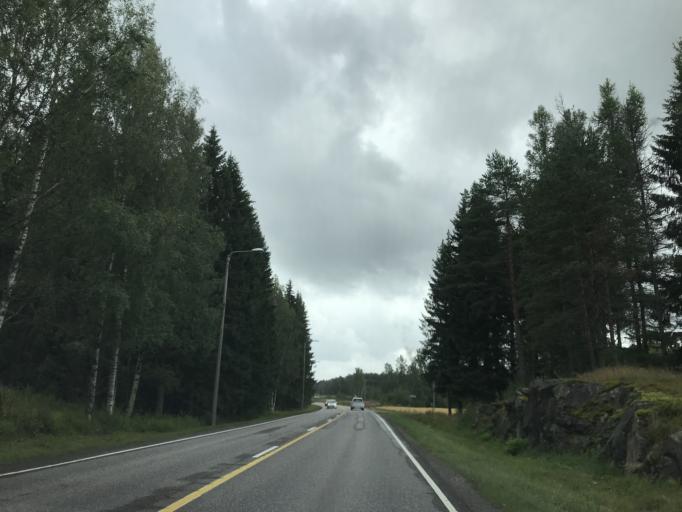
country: FI
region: Uusimaa
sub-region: Raaseporin
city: Ekenaes
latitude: 60.0026
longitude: 23.4023
